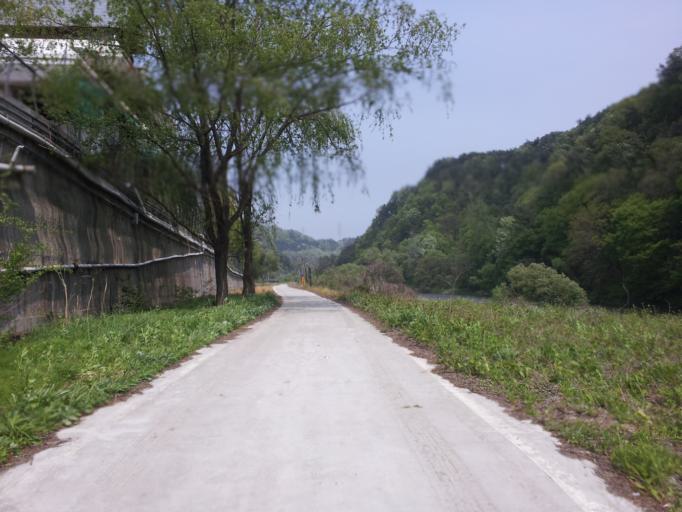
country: KR
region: Daejeon
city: Daejeon
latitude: 36.2617
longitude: 127.2874
